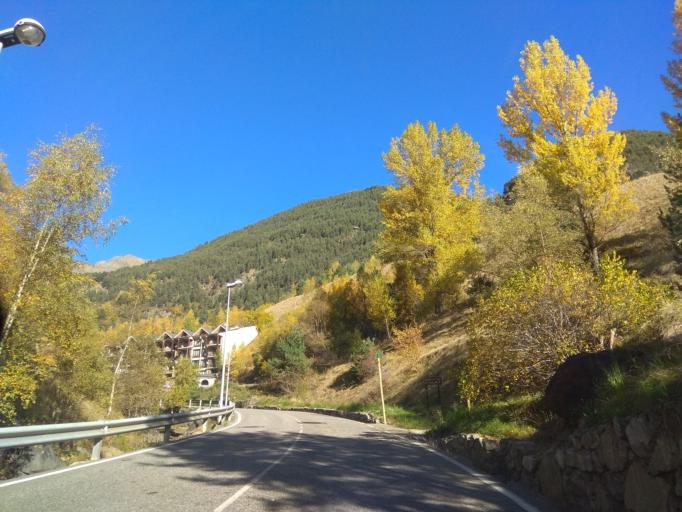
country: AD
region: La Massana
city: Arinsal
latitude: 42.5769
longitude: 1.4809
